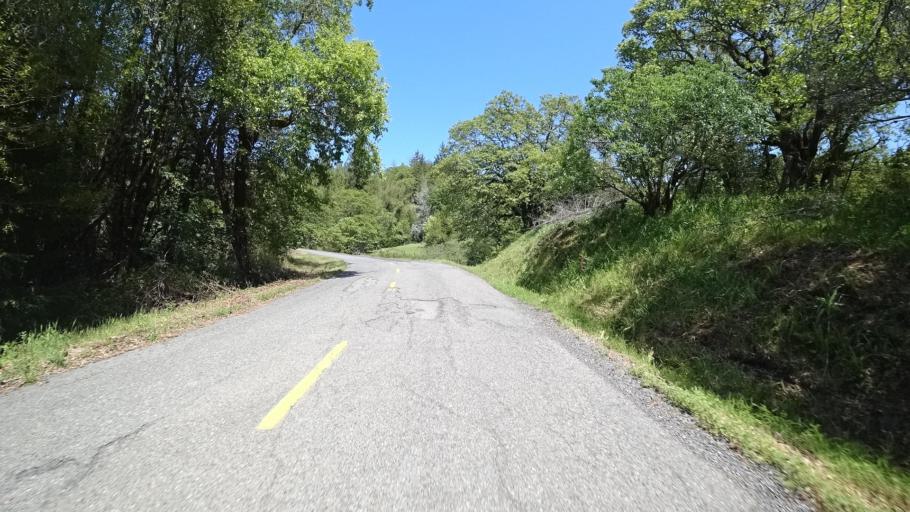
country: US
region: California
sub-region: Humboldt County
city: Redway
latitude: 40.2674
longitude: -123.6259
